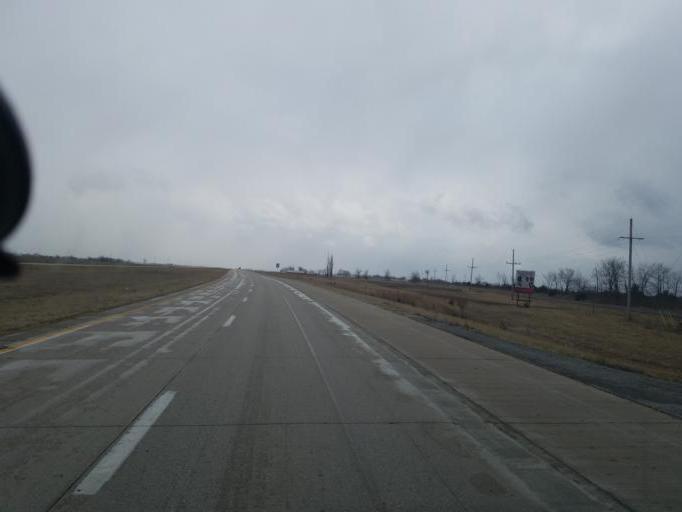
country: US
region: Missouri
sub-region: Randolph County
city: Moberly
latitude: 39.5326
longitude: -92.4452
